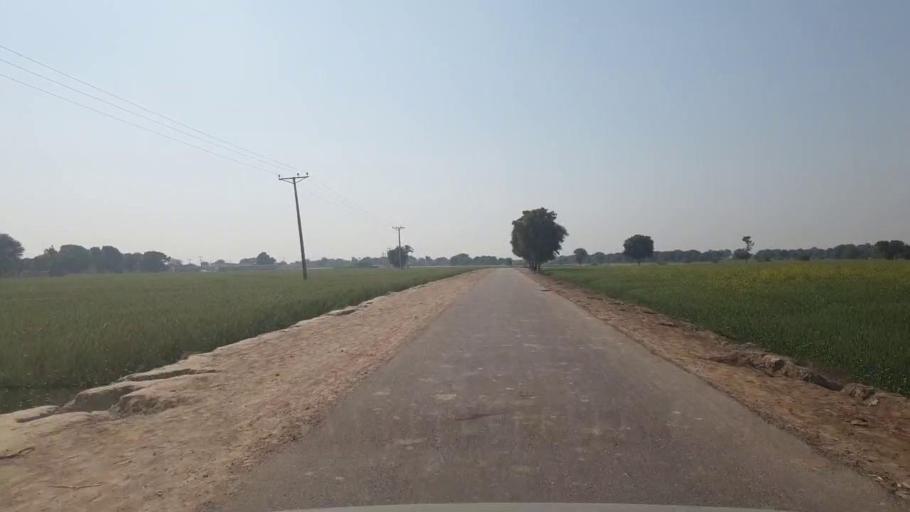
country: PK
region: Sindh
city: Chambar
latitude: 25.2505
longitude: 68.8314
